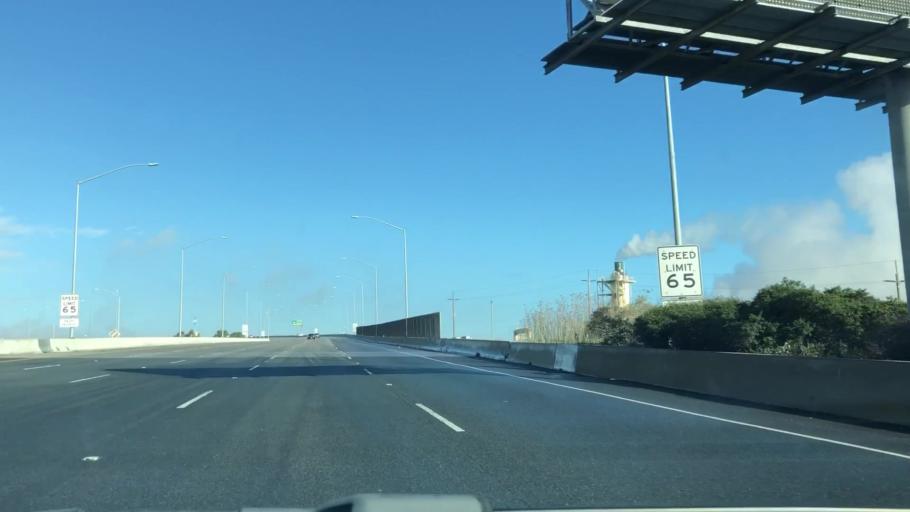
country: US
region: California
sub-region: Contra Costa County
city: Martinez
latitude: 38.0314
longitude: -122.1167
